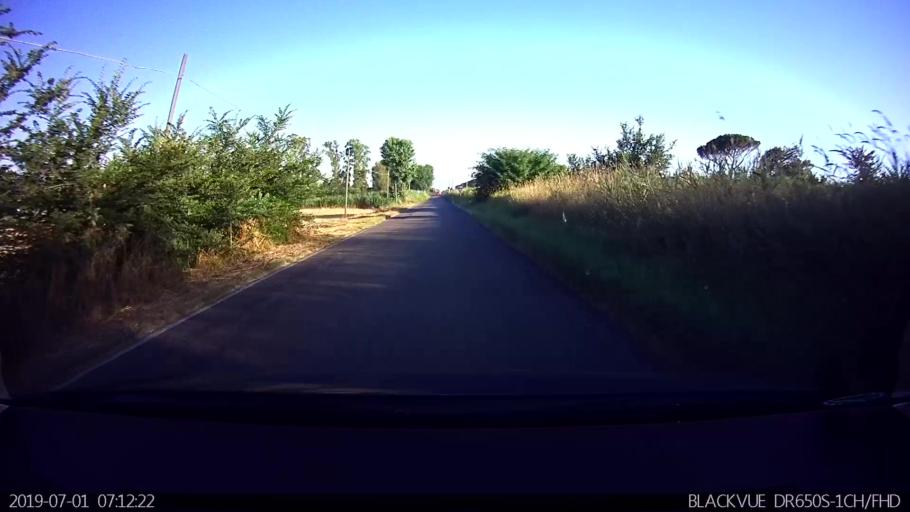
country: IT
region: Latium
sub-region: Provincia di Latina
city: Borgo Hermada
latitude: 41.3296
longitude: 13.1728
